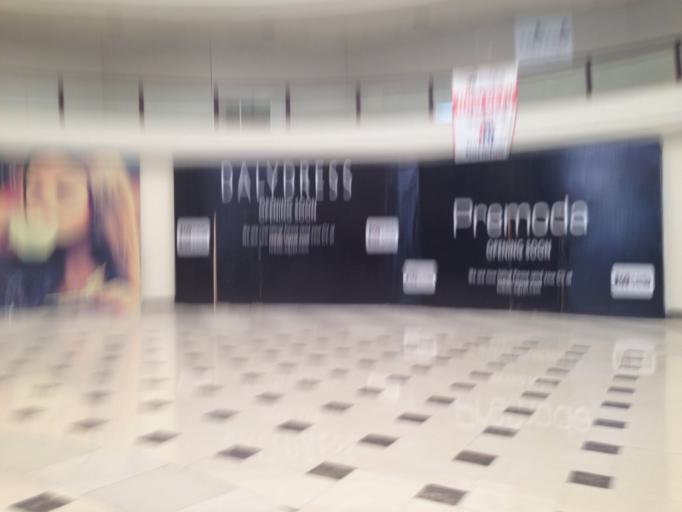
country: EG
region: Muhafazat al Qalyubiyah
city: Al Khankah
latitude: 30.0641
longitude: 31.4238
